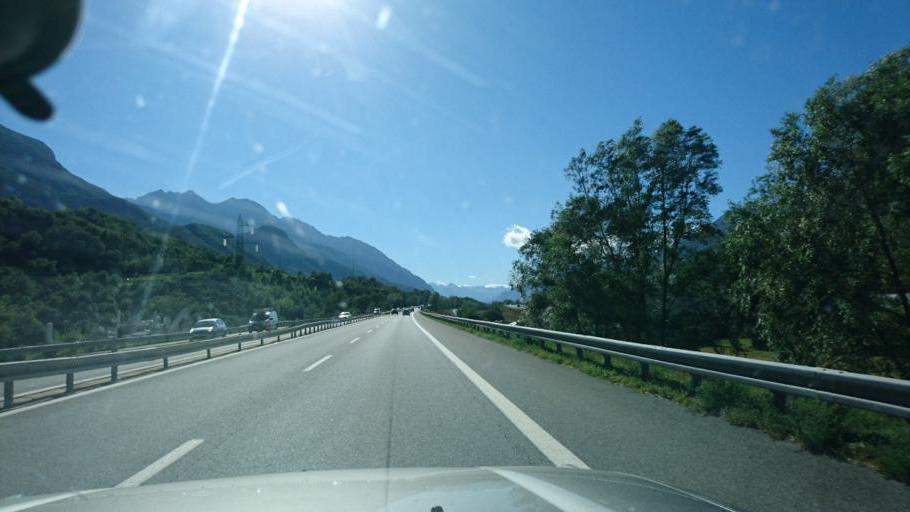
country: IT
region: Aosta Valley
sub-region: Valle d'Aosta
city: Chambave
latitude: 45.7431
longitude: 7.5581
